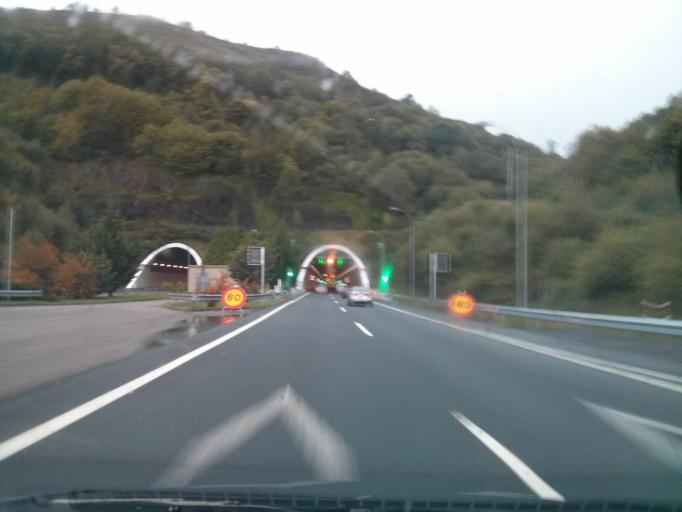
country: ES
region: Galicia
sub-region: Provincia de Pontevedra
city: Covelo
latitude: 42.1800
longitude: -8.3375
